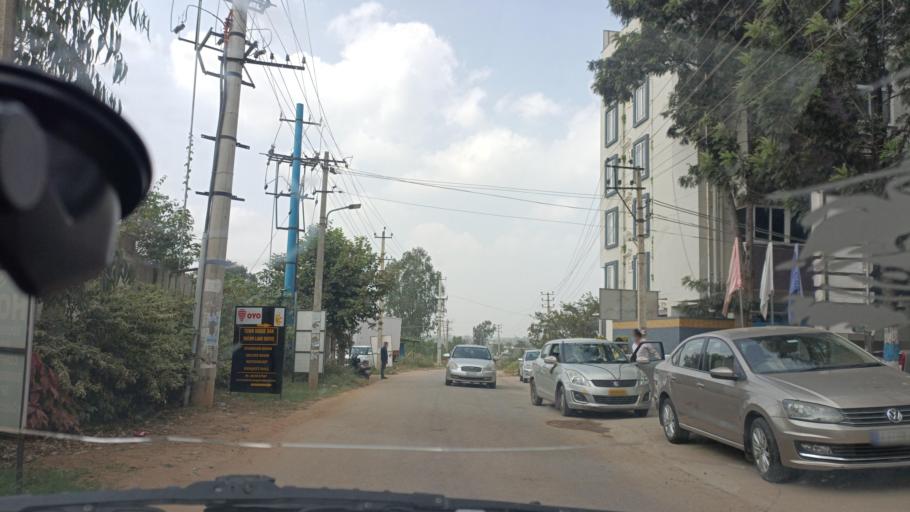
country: IN
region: Karnataka
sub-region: Bangalore Urban
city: Yelahanka
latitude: 13.1638
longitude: 77.6314
